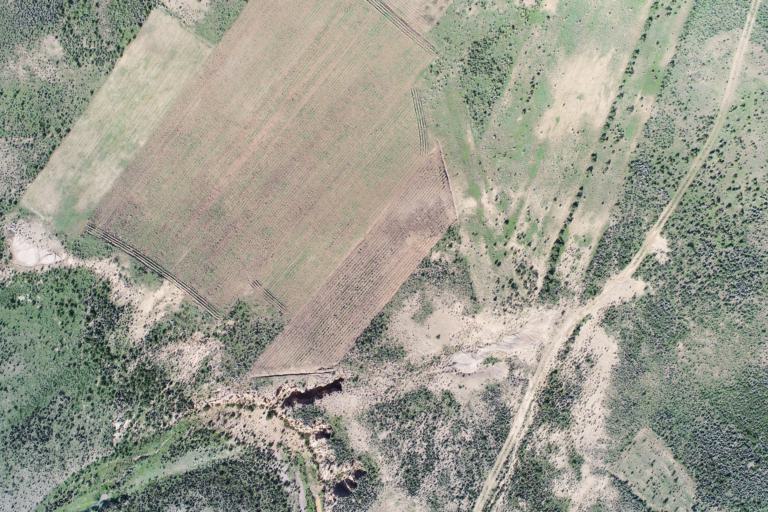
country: BO
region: La Paz
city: Curahuara de Carangas
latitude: -17.3015
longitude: -68.5231
